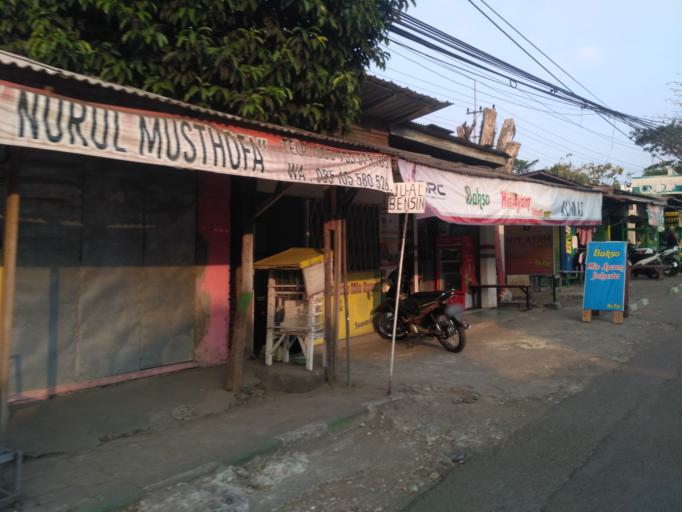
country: ID
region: East Java
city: Kepuh
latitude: -8.0038
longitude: 112.6179
